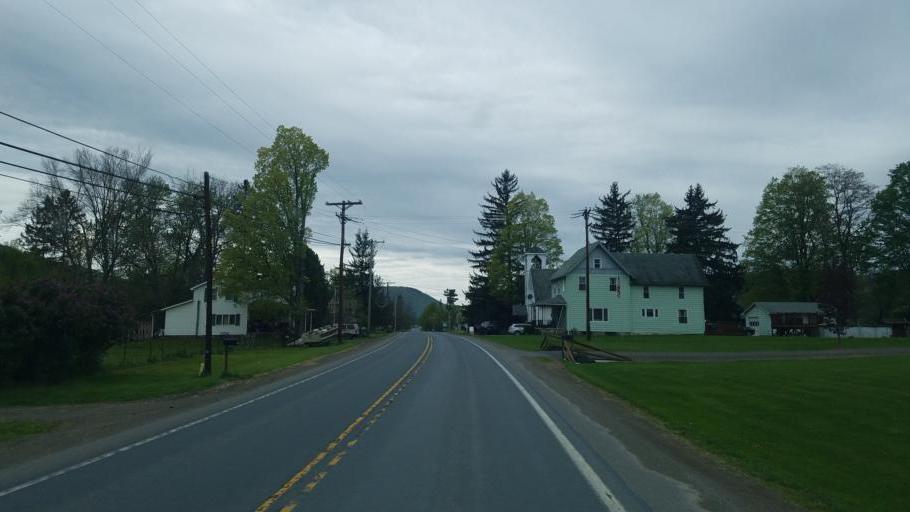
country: US
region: Pennsylvania
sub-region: Tioga County
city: Westfield
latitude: 41.9326
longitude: -77.4993
